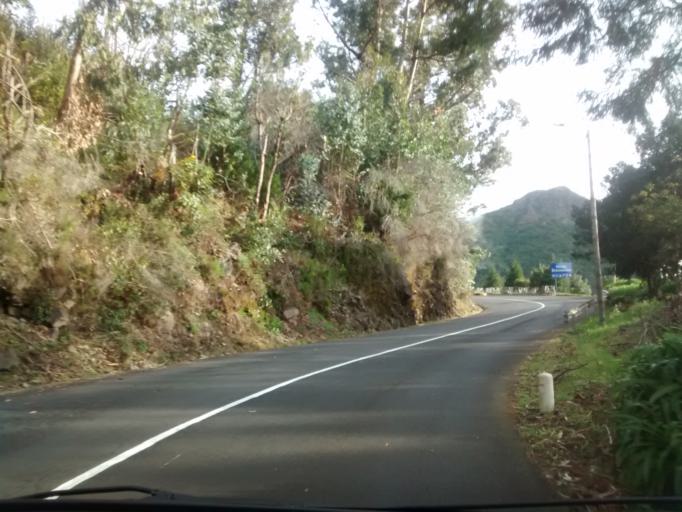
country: PT
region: Madeira
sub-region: Sao Vicente
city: Sao Vicente
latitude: 32.7482
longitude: -17.0257
